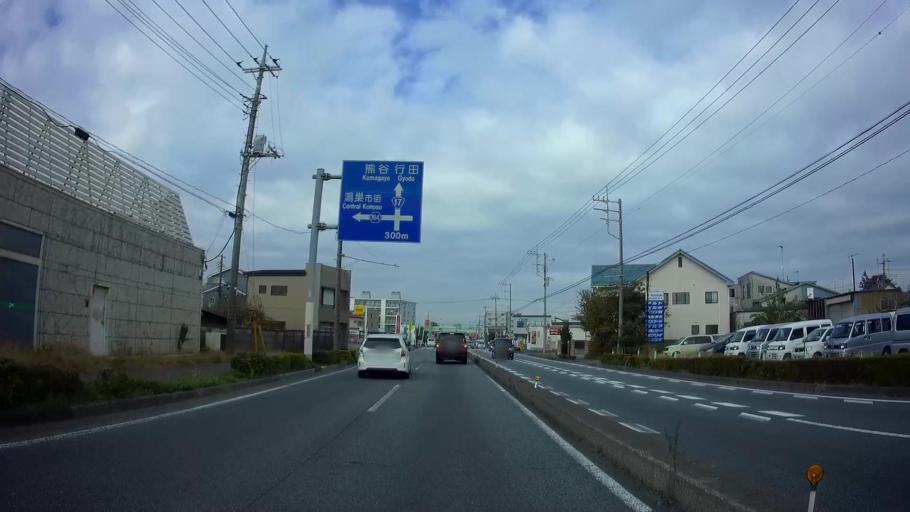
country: JP
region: Saitama
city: Konosu
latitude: 36.0694
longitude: 139.5048
